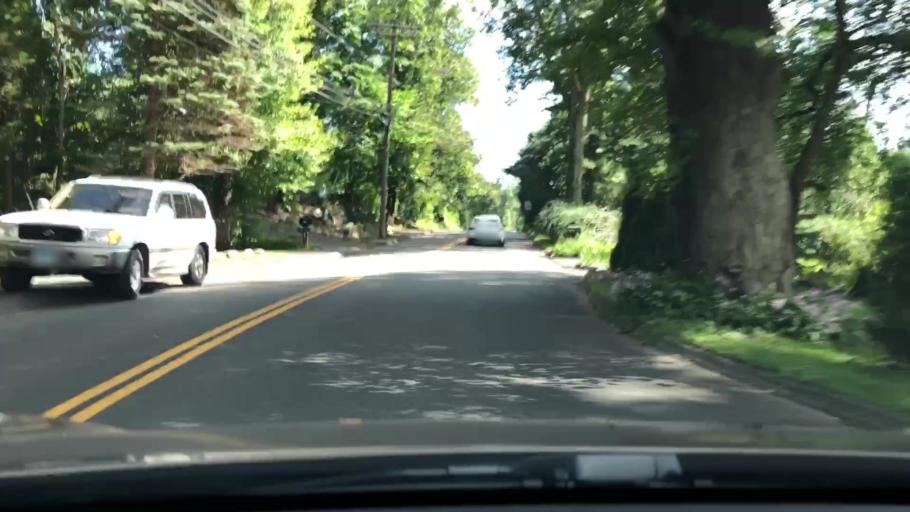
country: US
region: Connecticut
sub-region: Fairfield County
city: Norwalk
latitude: 41.1072
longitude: -73.4441
